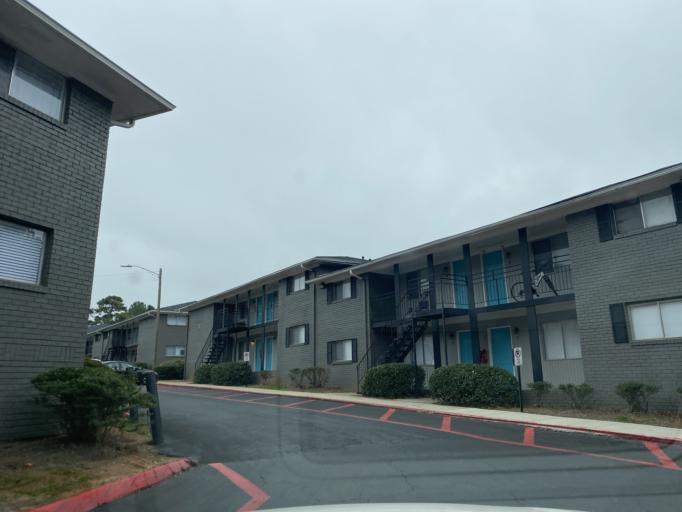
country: US
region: Georgia
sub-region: Cobb County
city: Fair Oaks
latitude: 33.9057
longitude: -84.5683
